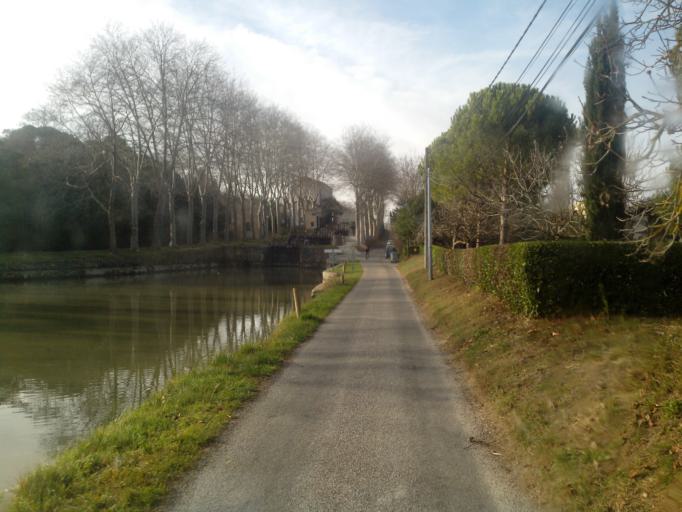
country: FR
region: Languedoc-Roussillon
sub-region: Departement de l'Aude
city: Castelnaudary
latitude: 43.3117
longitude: 1.9632
